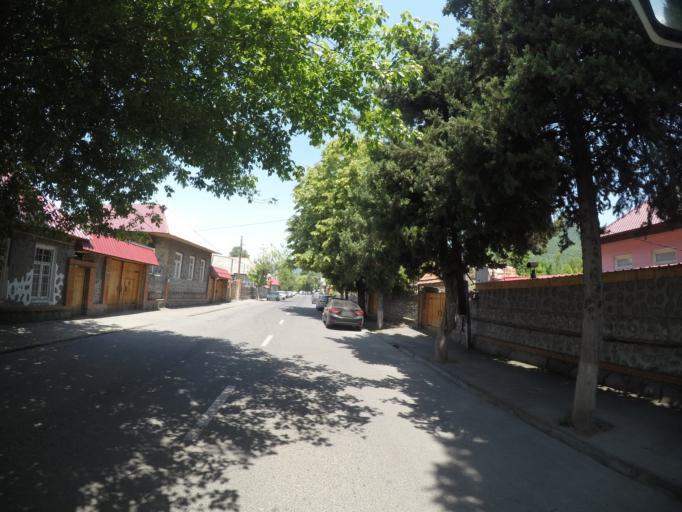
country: AZ
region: Qakh Rayon
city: Qax
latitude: 41.4183
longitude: 46.9188
